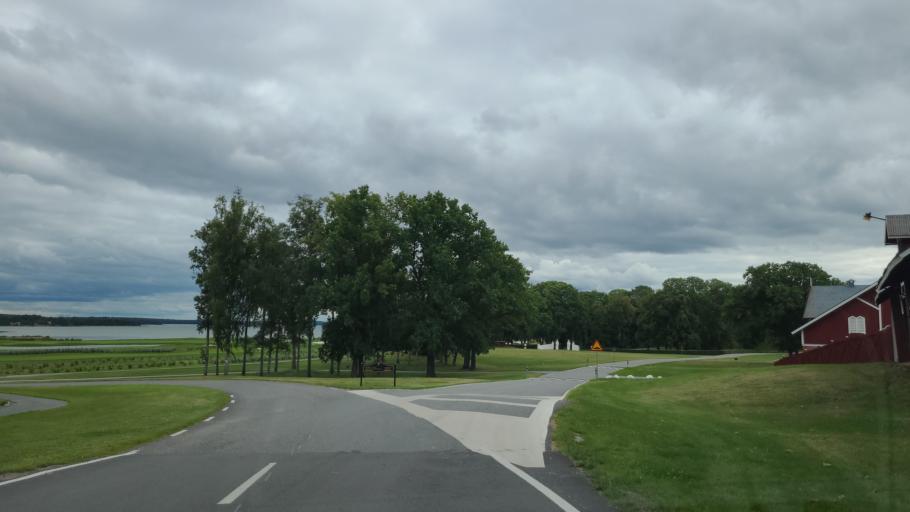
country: SE
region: Stockholm
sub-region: Upplands-Bro Kommun
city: Bro
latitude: 59.4999
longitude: 17.6271
